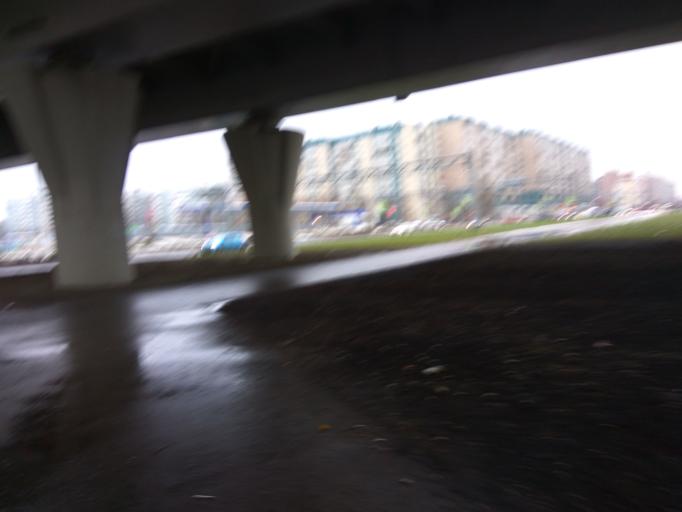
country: RU
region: St.-Petersburg
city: Staraya Derevnya
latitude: 60.0040
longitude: 30.2328
